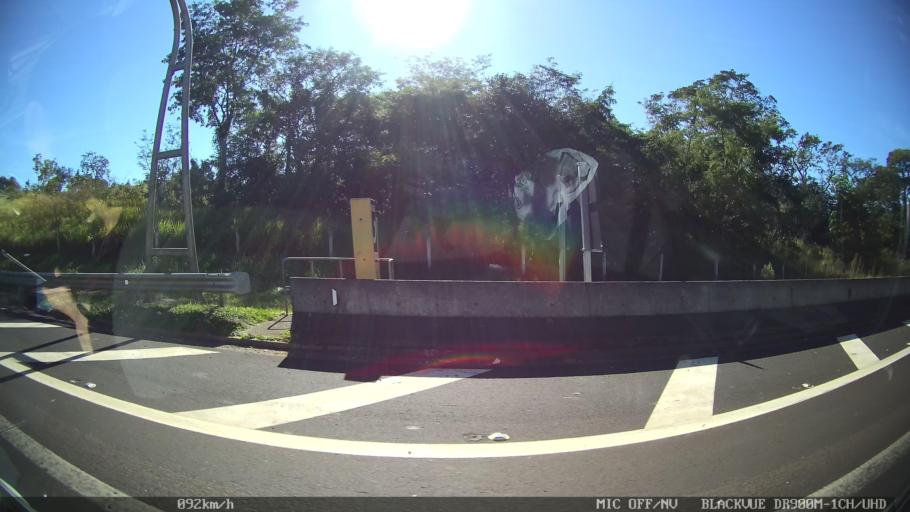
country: BR
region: Sao Paulo
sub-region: Franca
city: Franca
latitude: -20.5652
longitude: -47.4094
